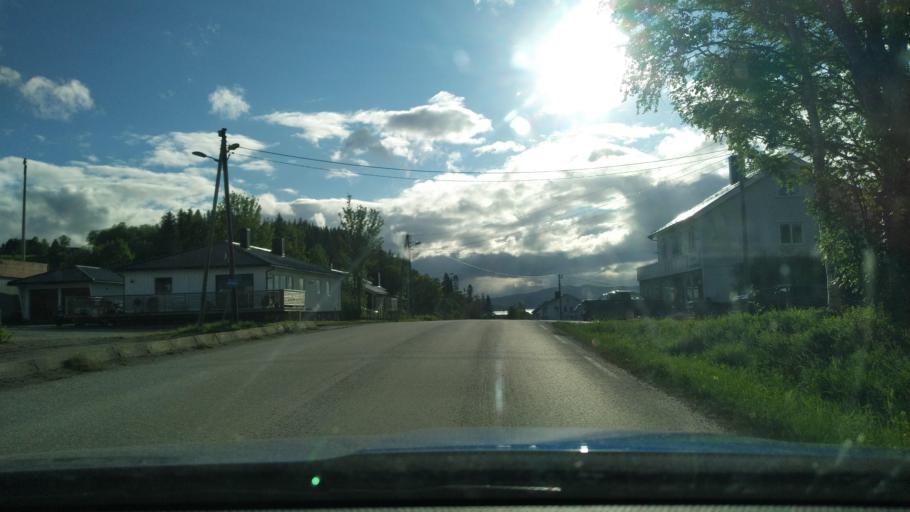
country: NO
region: Troms
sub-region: Sorreisa
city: Sorreisa
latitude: 69.1439
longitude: 18.1428
